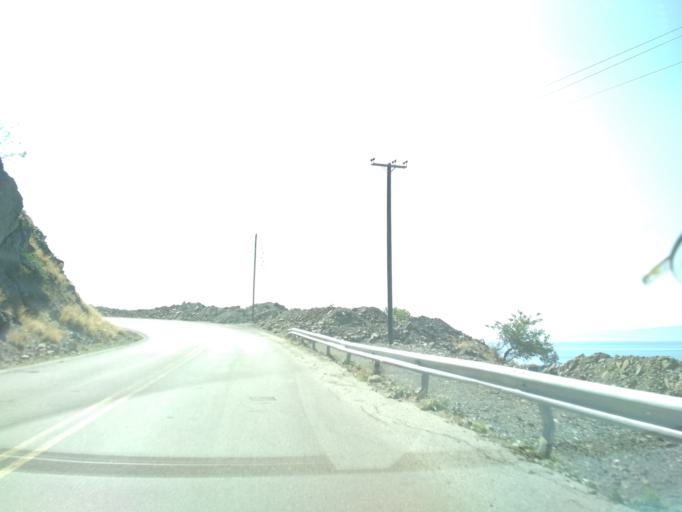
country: GR
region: Central Greece
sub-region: Nomos Evvoias
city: Roviai
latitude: 38.8476
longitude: 23.1572
